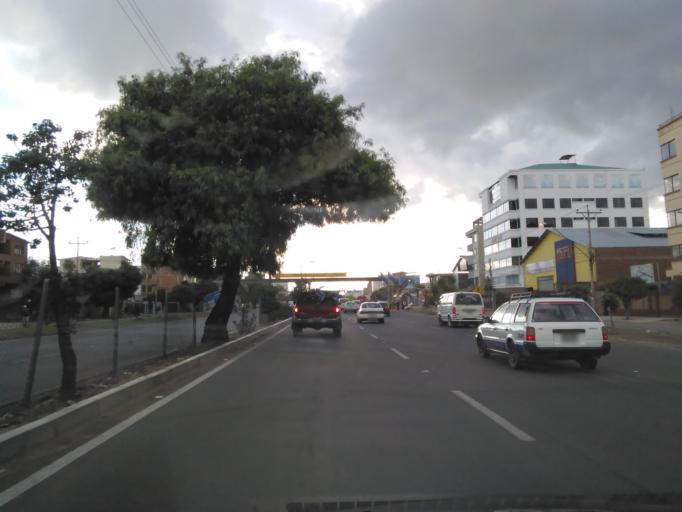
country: BO
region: Cochabamba
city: Cochabamba
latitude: -17.3926
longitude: -66.2016
